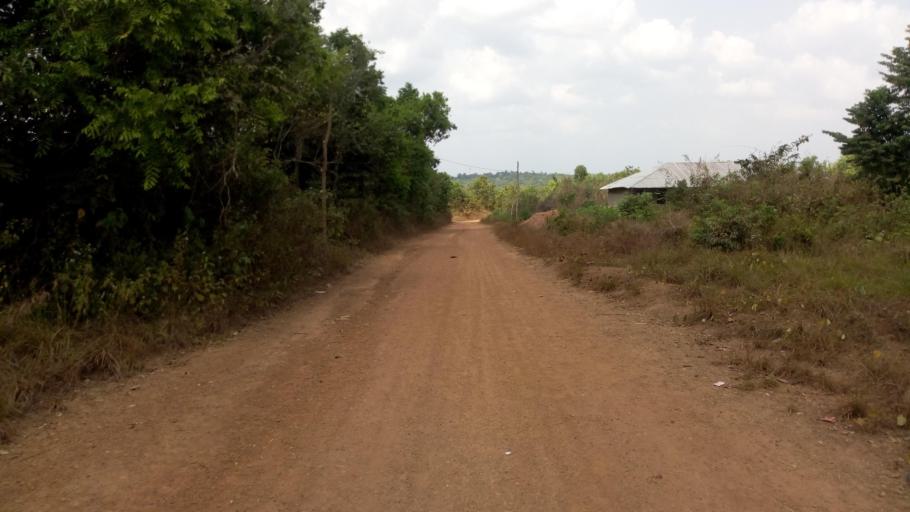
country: SL
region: Southern Province
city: Mogbwemo
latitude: 7.7930
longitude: -12.3073
